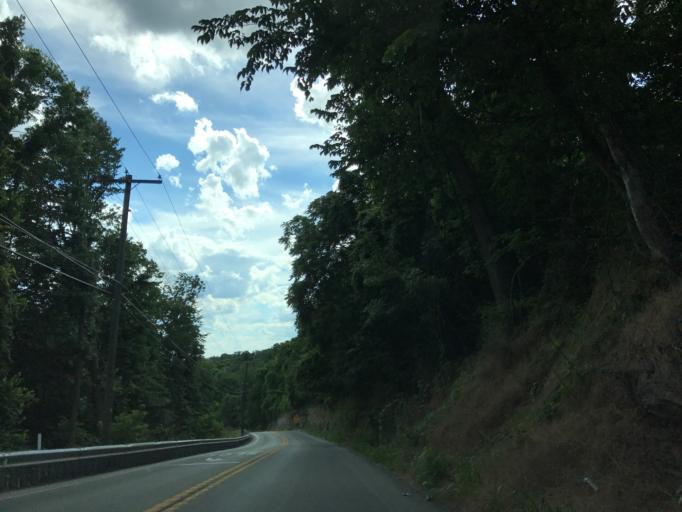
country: US
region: Pennsylvania
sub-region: Lancaster County
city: Conestoga
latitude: 39.9202
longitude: -76.3051
